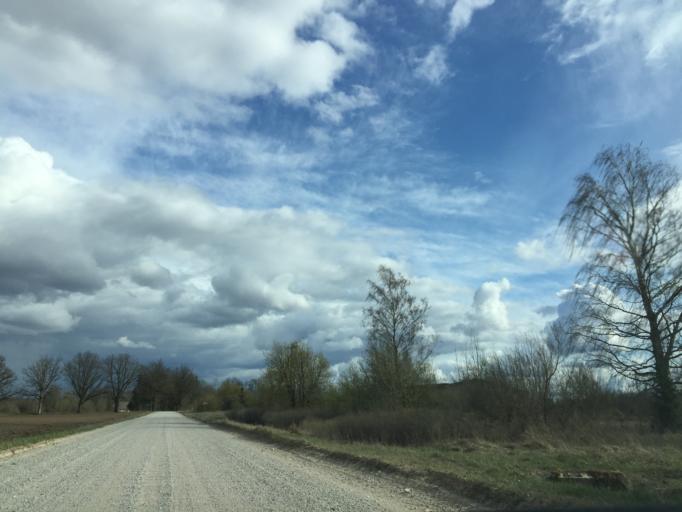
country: LV
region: Burtnieki
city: Matisi
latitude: 57.6178
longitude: 25.0739
